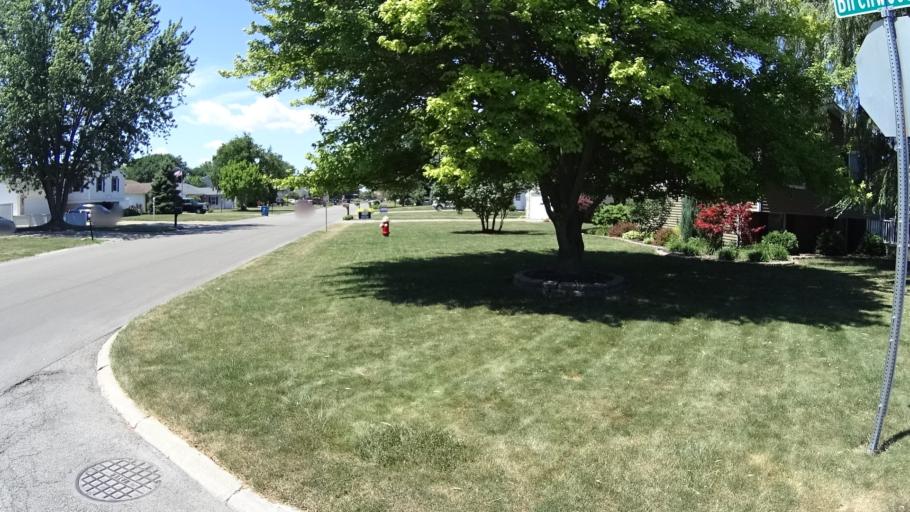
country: US
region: Ohio
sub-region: Erie County
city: Sandusky
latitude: 41.4086
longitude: -82.6886
